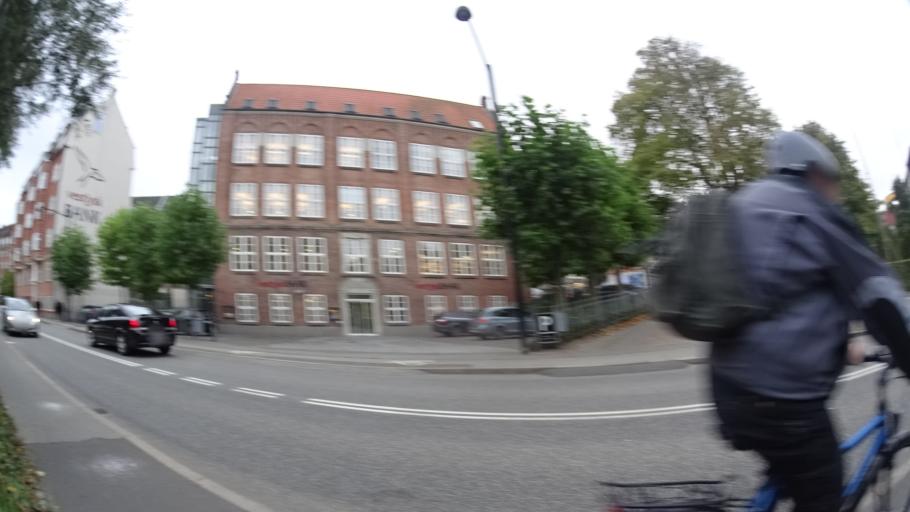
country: DK
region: Central Jutland
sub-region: Arhus Kommune
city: Arhus
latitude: 56.1555
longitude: 10.2022
